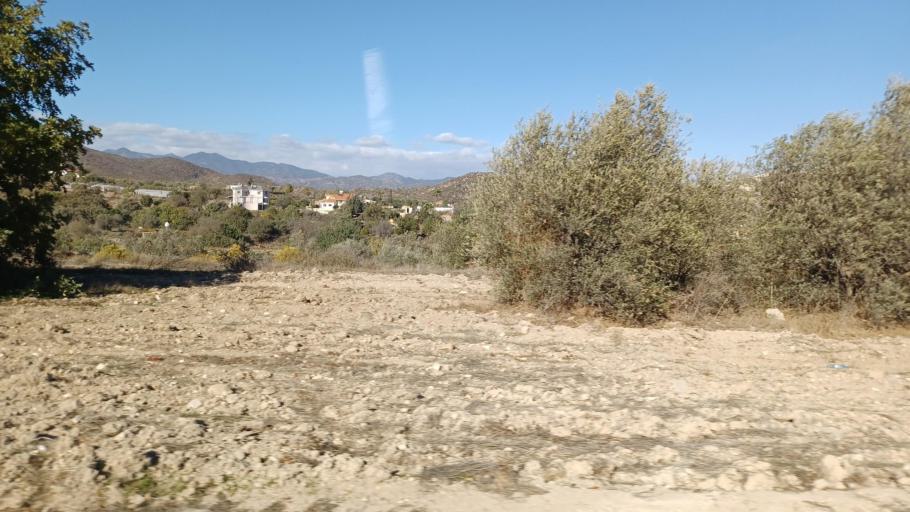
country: CY
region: Limassol
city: Pyrgos
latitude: 34.7773
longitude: 33.2499
